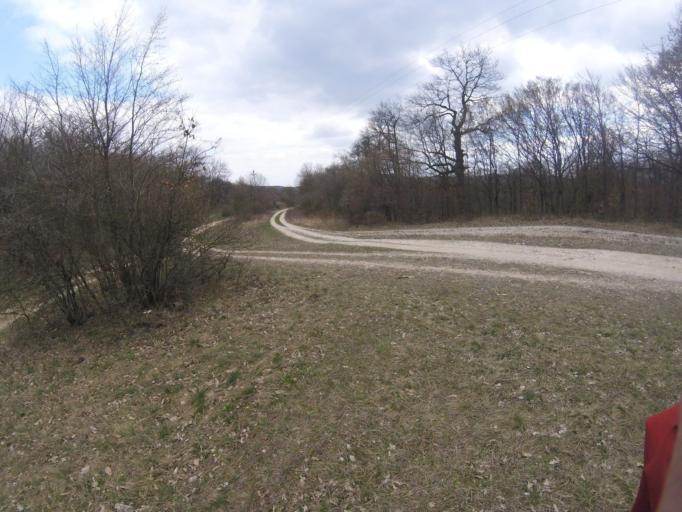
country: HU
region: Fejer
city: Csakvar
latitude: 47.4596
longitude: 18.4249
